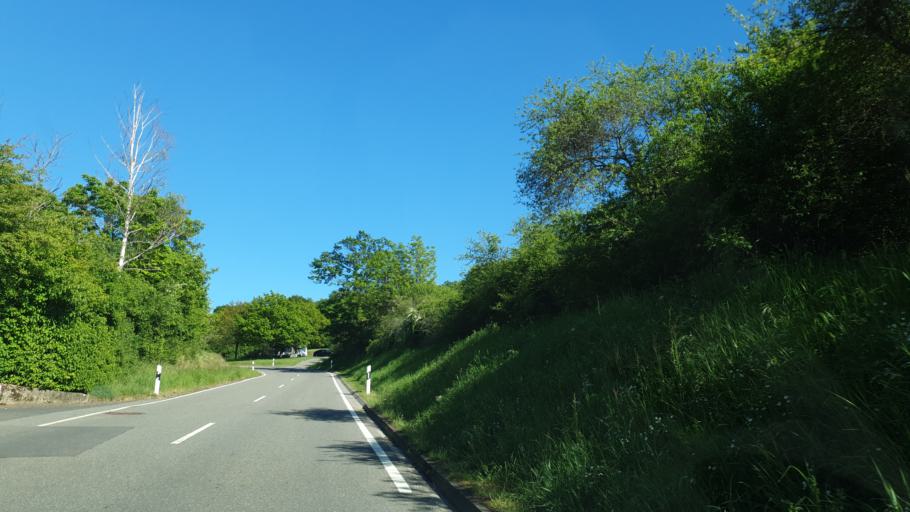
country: DE
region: Rheinland-Pfalz
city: Frucht
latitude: 50.3111
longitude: 7.6775
